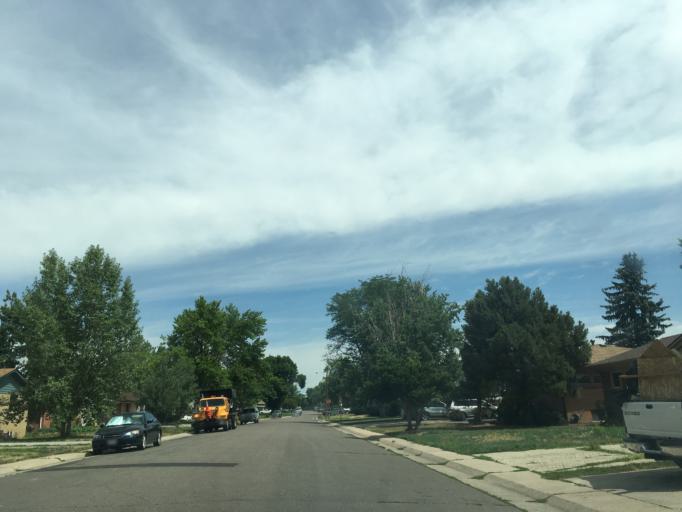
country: US
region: Colorado
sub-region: Arapahoe County
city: Sheridan
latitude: 39.6869
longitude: -105.0412
